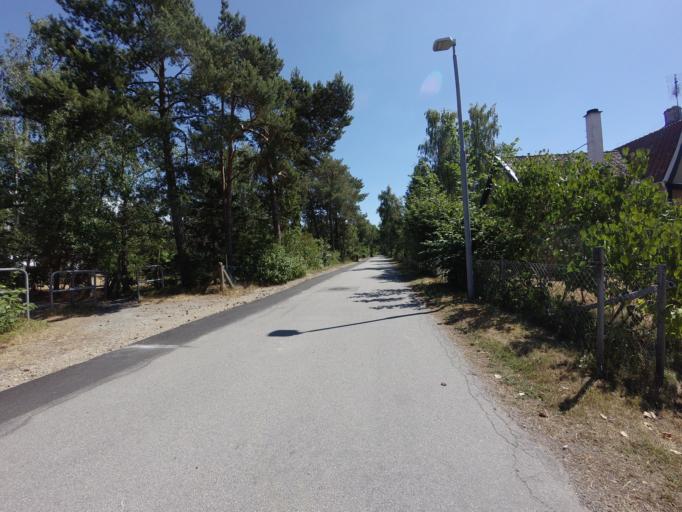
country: SE
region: Skane
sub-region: Vellinge Kommun
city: Ljunghusen
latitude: 55.4020
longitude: 12.9377
